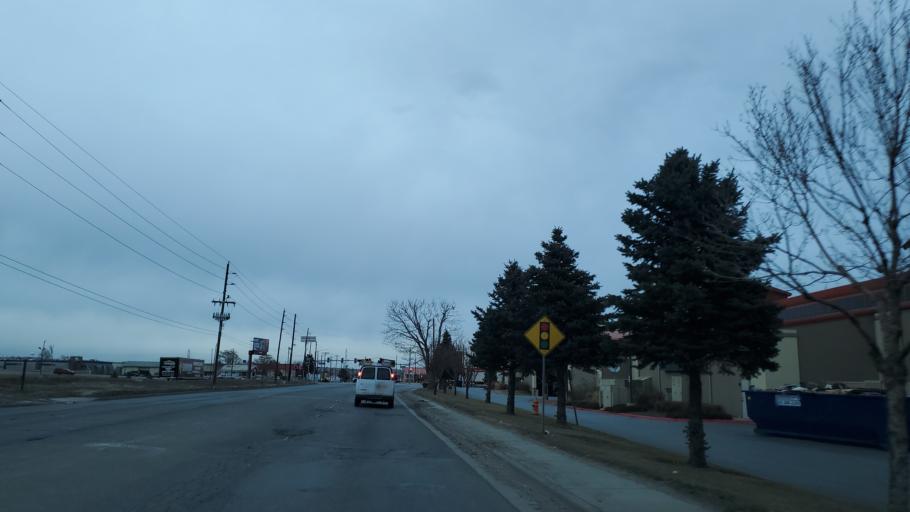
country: US
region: Colorado
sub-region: Adams County
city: Twin Lakes
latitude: 39.7997
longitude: -104.9874
